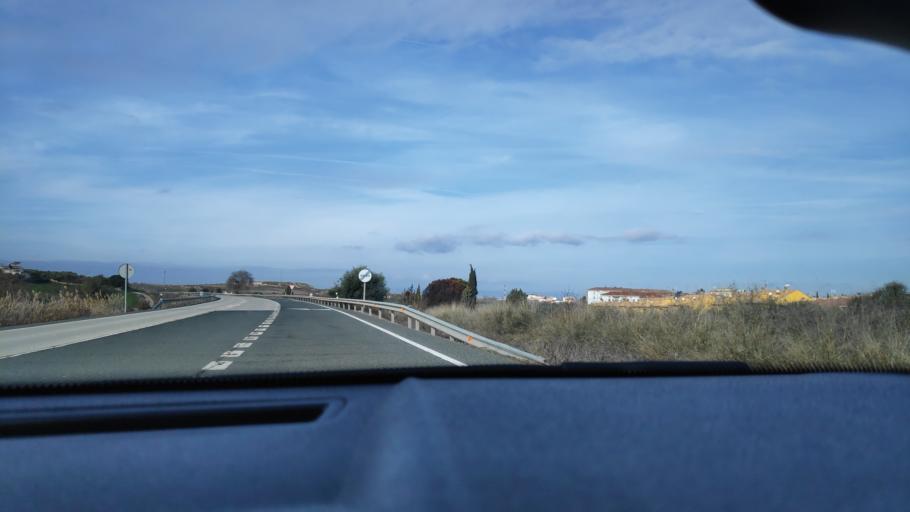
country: ES
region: Andalusia
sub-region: Provincia de Jaen
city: Linares
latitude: 38.0822
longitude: -3.6227
